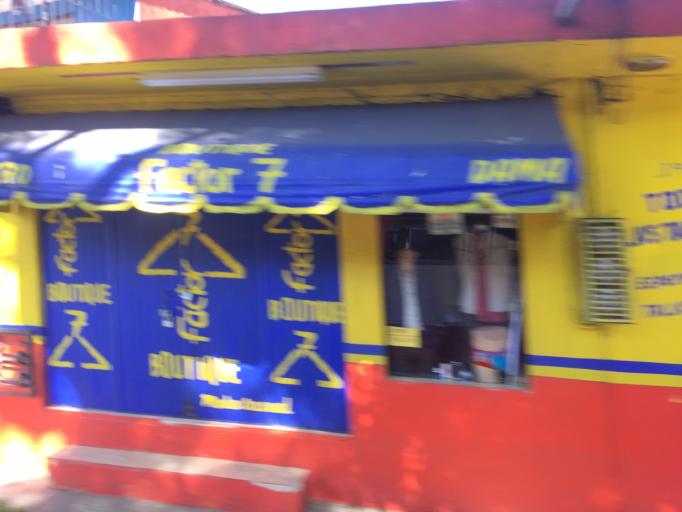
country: MX
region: Veracruz
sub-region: Xalapa
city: Xalapa de Enriquez
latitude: 19.5341
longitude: -96.9088
